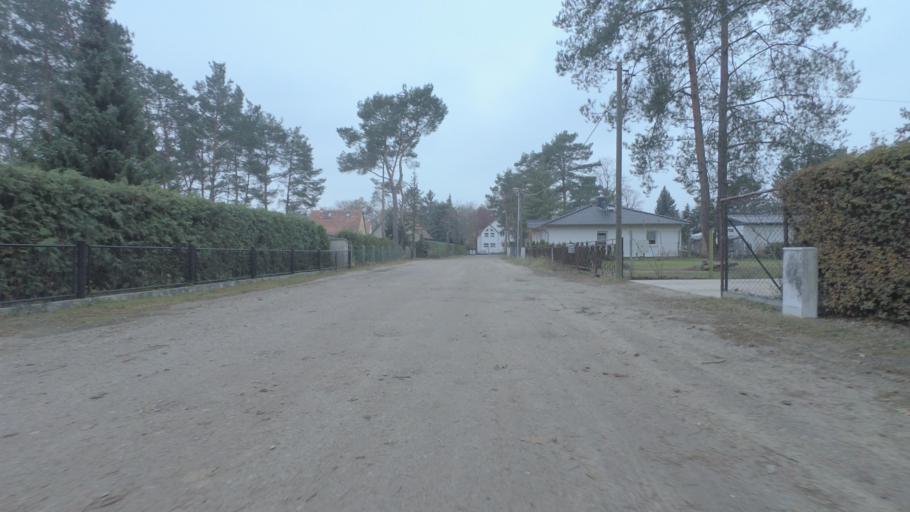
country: DE
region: Brandenburg
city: Am Mellensee
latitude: 52.1673
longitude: 13.3960
